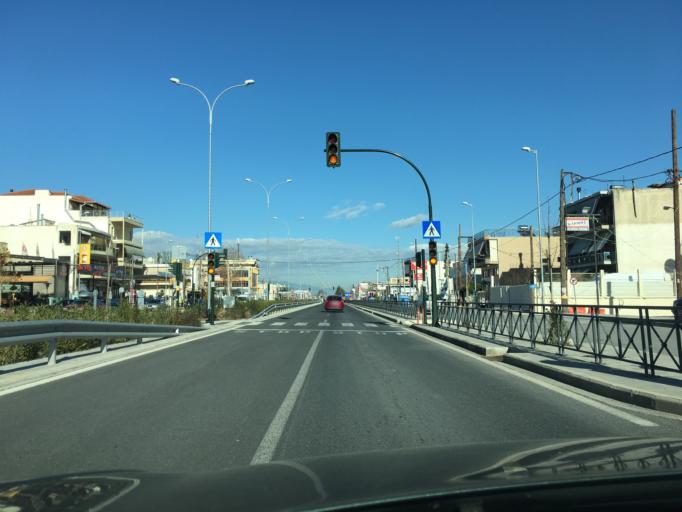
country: GR
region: Thessaly
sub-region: Nomos Larisis
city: Larisa
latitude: 39.6242
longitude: 22.4310
